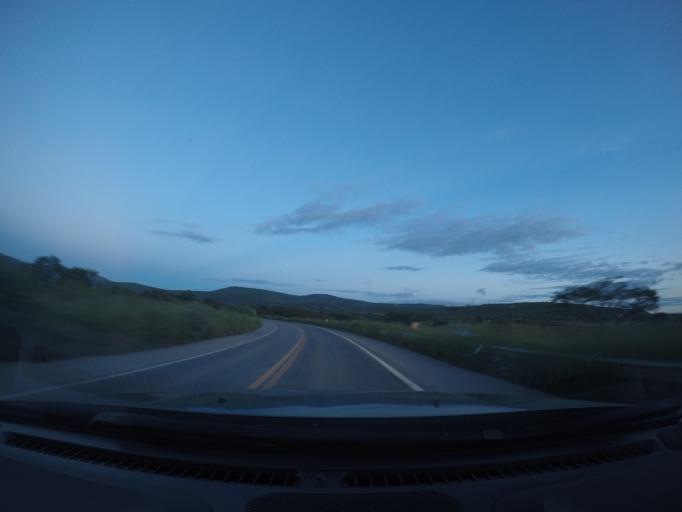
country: BR
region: Bahia
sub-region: Seabra
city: Seabra
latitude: -12.4891
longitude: -41.7318
